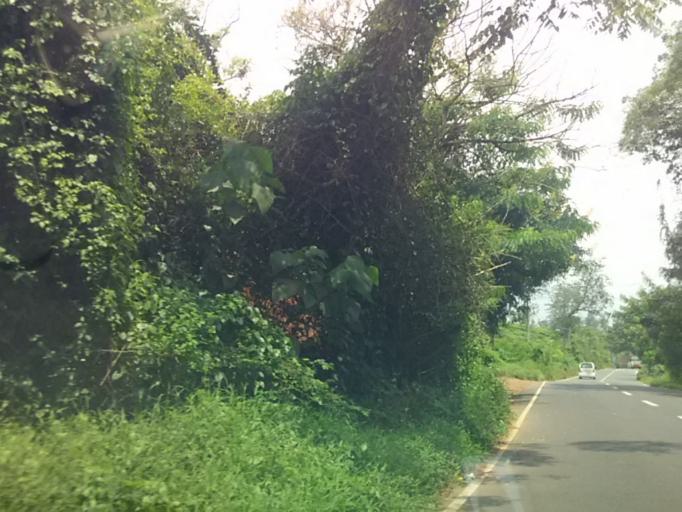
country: IN
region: Kerala
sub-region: Wayanad
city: Kalpetta
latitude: 11.5734
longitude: 76.0487
